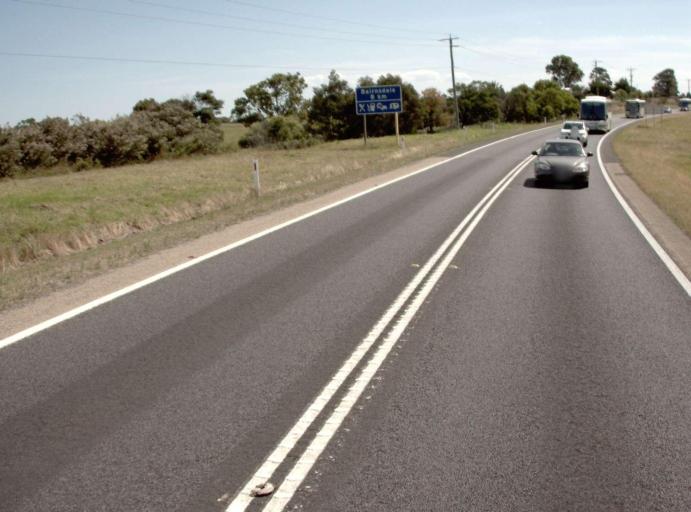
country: AU
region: Victoria
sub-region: East Gippsland
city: Bairnsdale
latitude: -37.8257
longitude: 147.7174
